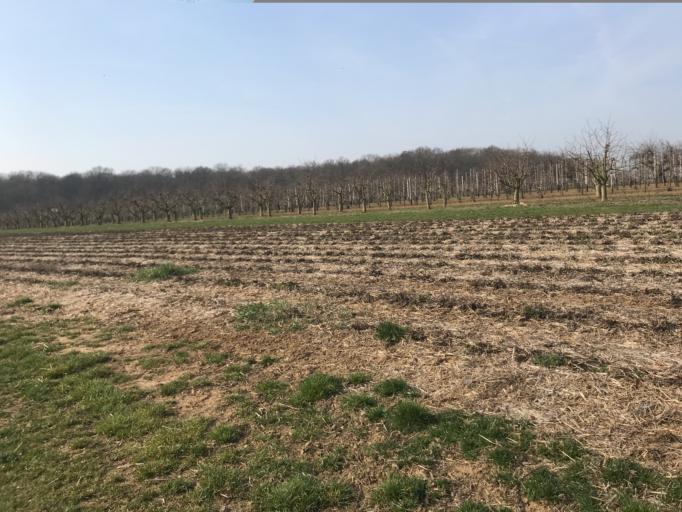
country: DE
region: Rheinland-Pfalz
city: Ober-Olm
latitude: 49.9693
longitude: 8.1822
